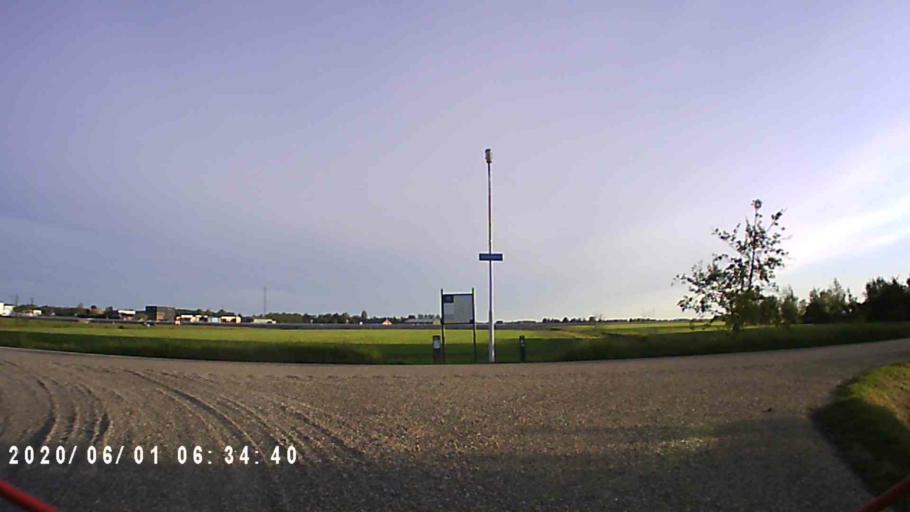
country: NL
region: Friesland
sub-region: Gemeente Kollumerland en Nieuwkruisland
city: Kollum
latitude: 53.2800
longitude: 6.1660
